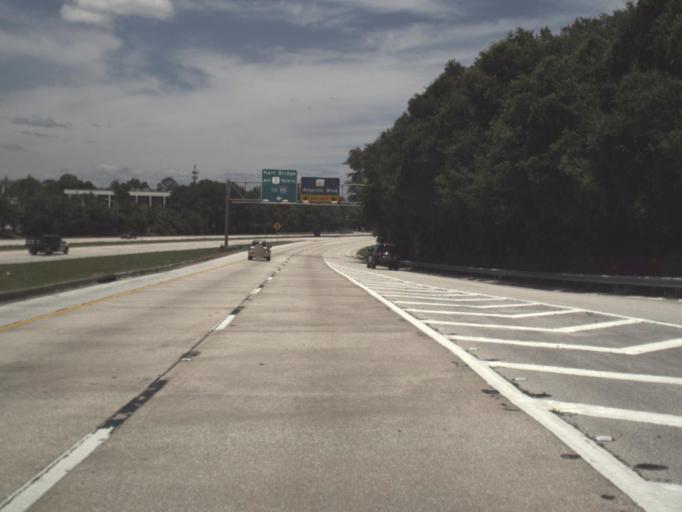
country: US
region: Florida
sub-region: Duval County
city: Jacksonville
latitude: 30.3040
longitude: -81.6132
